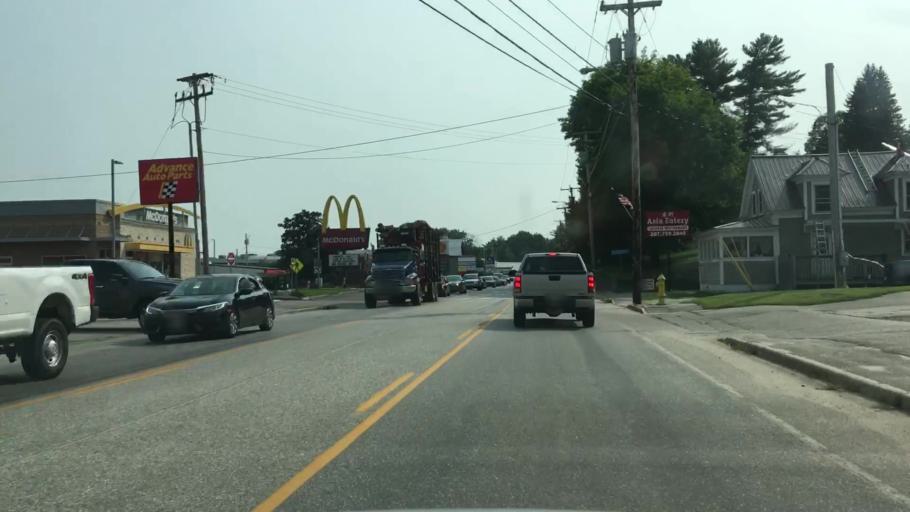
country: US
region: Maine
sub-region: Oxford County
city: South Paris
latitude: 44.2177
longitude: -70.5173
